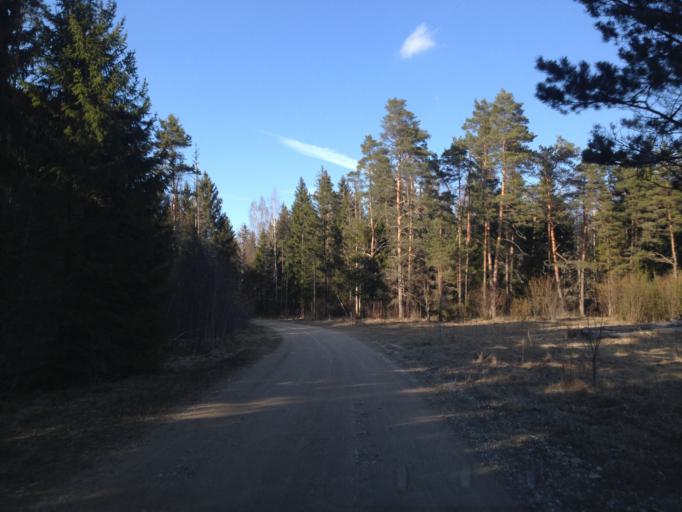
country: EE
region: Harju
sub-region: Nissi vald
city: Turba
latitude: 59.1187
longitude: 24.1614
